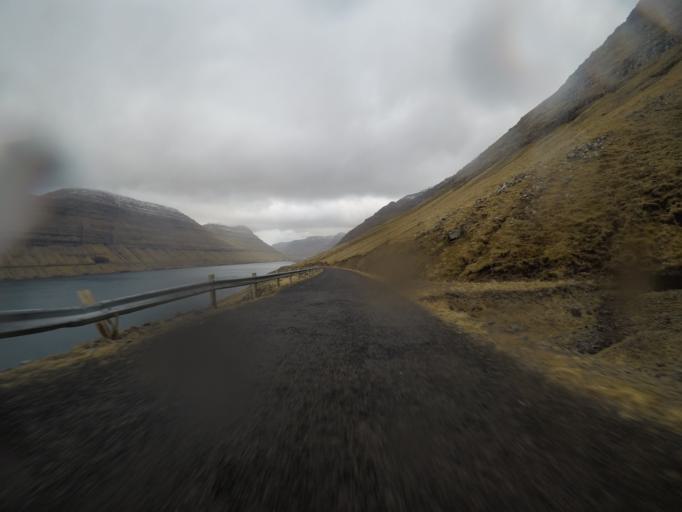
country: FO
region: Nordoyar
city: Klaksvik
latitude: 62.3278
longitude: -6.5680
